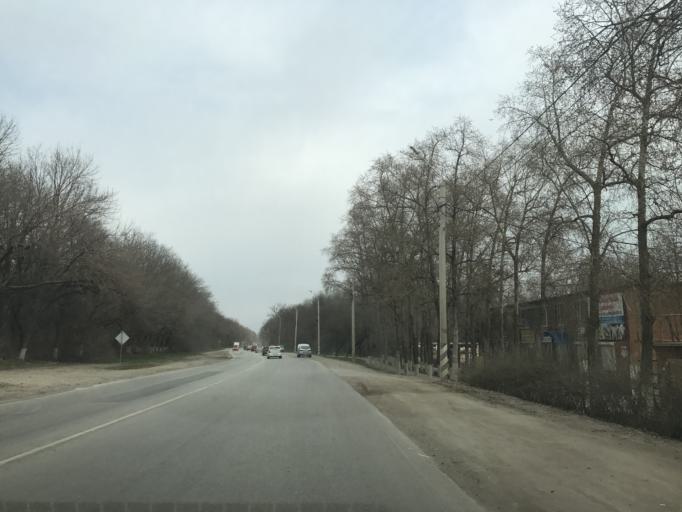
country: RU
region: Rostov
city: Aksay
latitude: 47.2737
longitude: 39.8784
